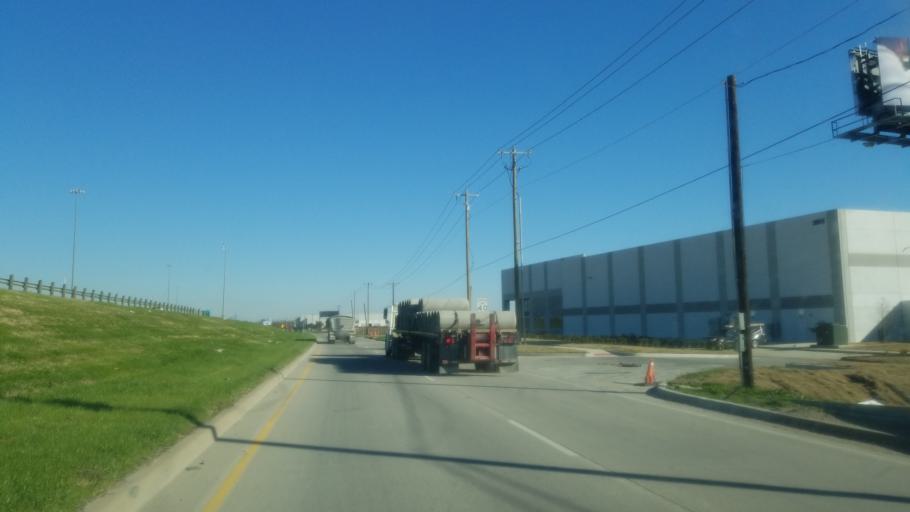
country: US
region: Texas
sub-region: Dallas County
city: Grand Prairie
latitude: 32.7617
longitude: -96.9518
